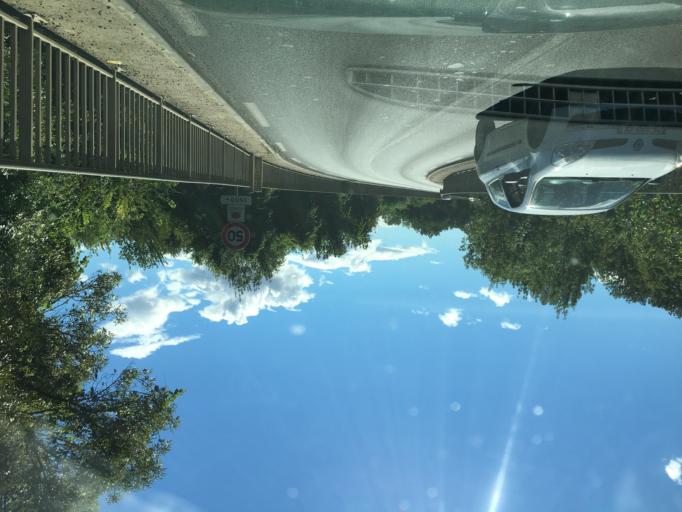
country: FR
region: Languedoc-Roussillon
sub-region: Departement de l'Herault
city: Florensac
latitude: 43.3842
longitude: 3.4597
